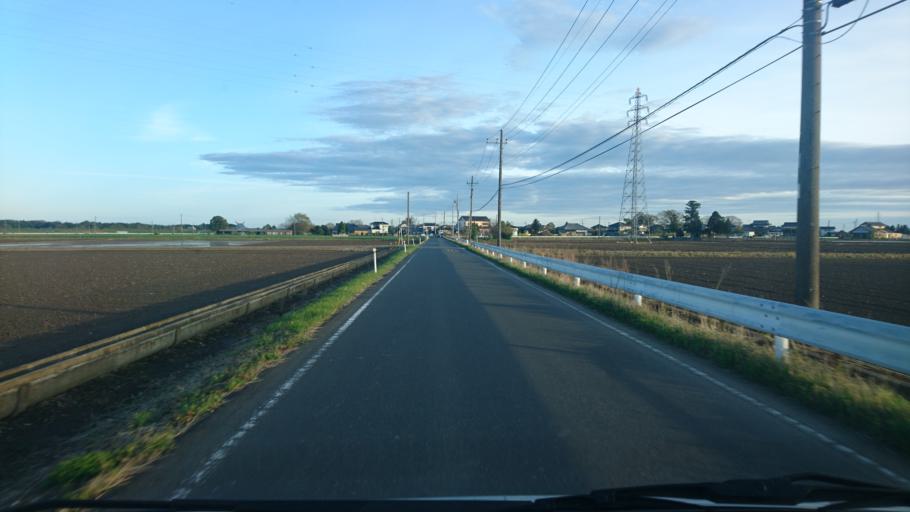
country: JP
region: Ibaraki
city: Ishige
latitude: 36.1011
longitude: 139.9930
